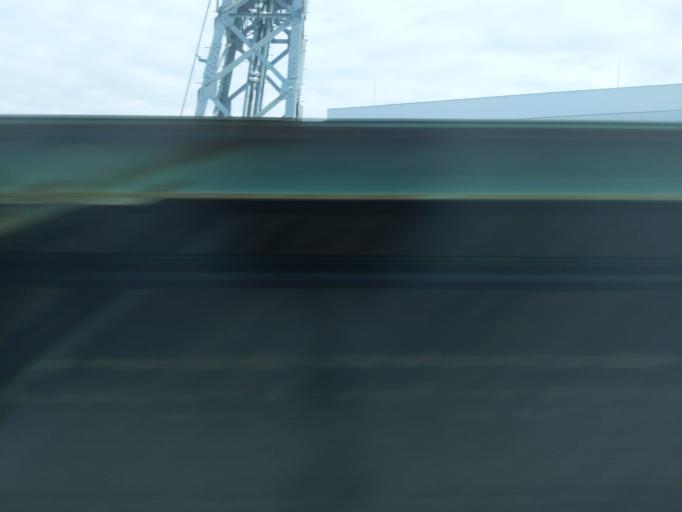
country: JP
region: Tochigi
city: Oyama
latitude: 36.2704
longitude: 139.7746
